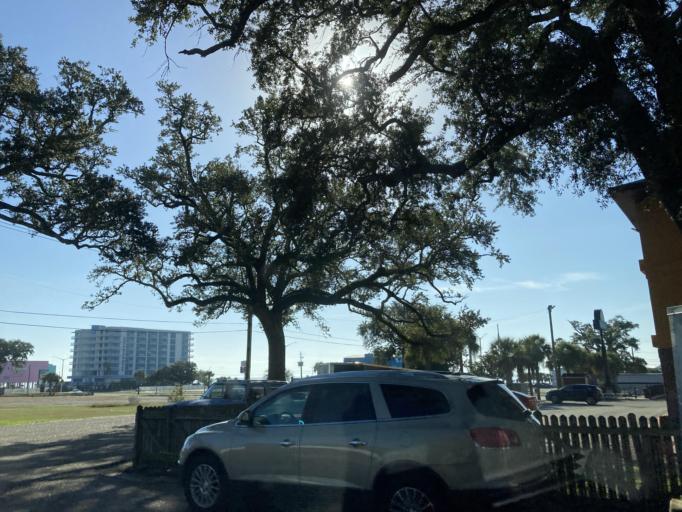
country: US
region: Mississippi
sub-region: Harrison County
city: Biloxi
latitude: 30.3948
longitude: -88.9433
